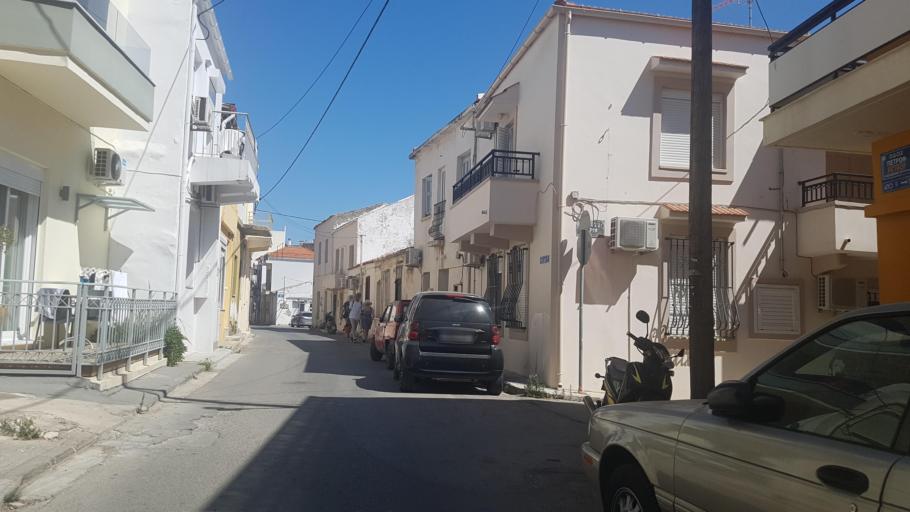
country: GR
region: Crete
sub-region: Nomos Chanias
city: Chania
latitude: 35.5141
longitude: 24.0104
